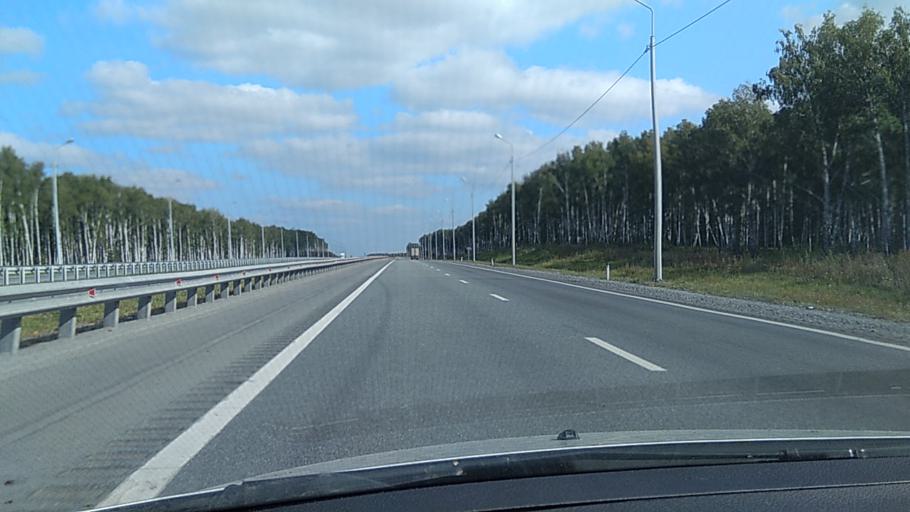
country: RU
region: Chelyabinsk
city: Chebarkul'
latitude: 54.9120
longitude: 60.3975
